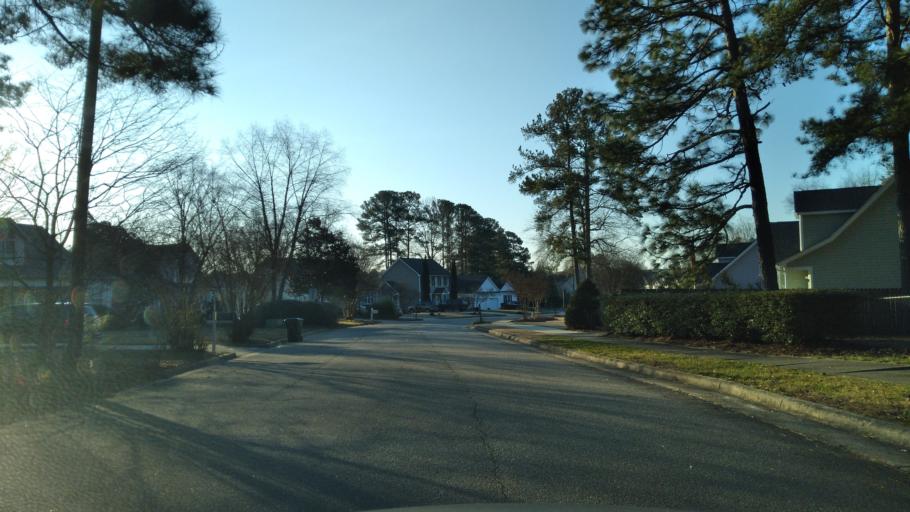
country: US
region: North Carolina
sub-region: Wake County
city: Garner
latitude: 35.6970
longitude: -78.6140
